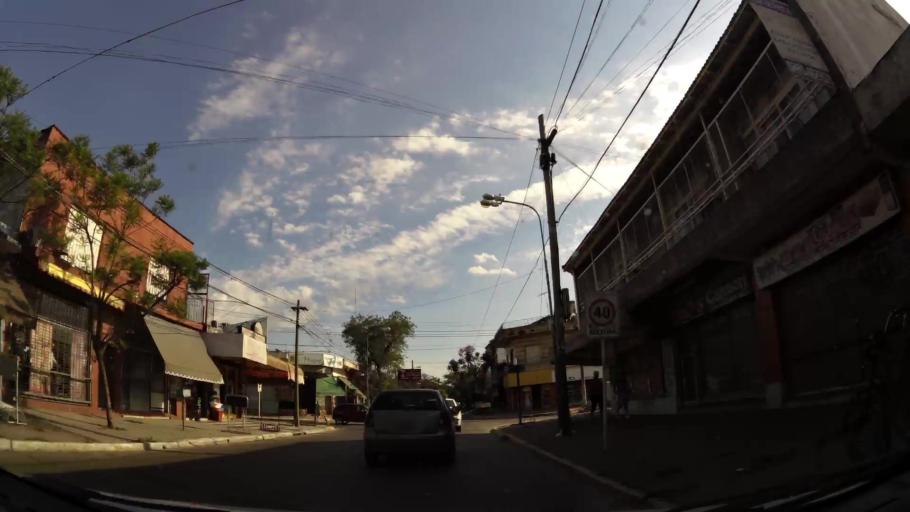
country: AR
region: Buenos Aires
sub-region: Partido de Merlo
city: Merlo
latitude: -34.6599
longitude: -58.7257
